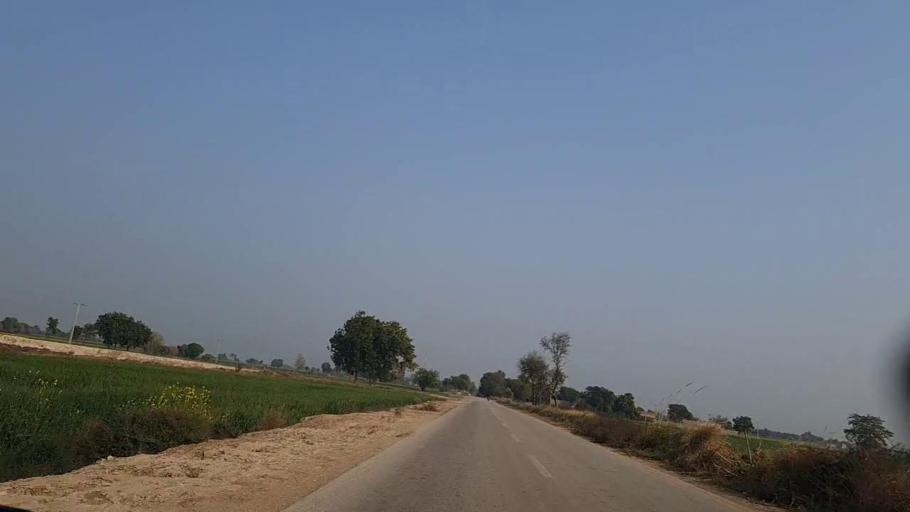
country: PK
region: Sindh
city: Sakrand
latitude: 26.1335
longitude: 68.2032
